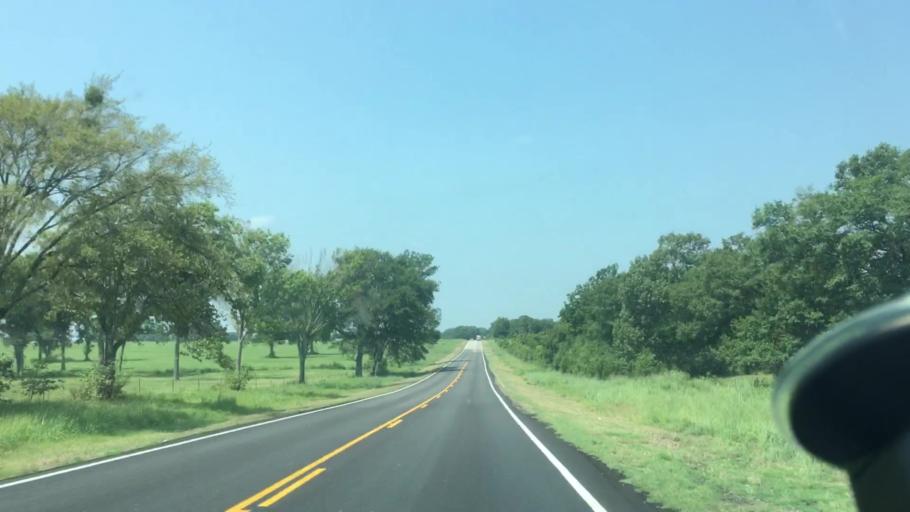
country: US
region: Oklahoma
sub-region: Atoka County
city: Atoka
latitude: 34.2787
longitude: -95.9385
